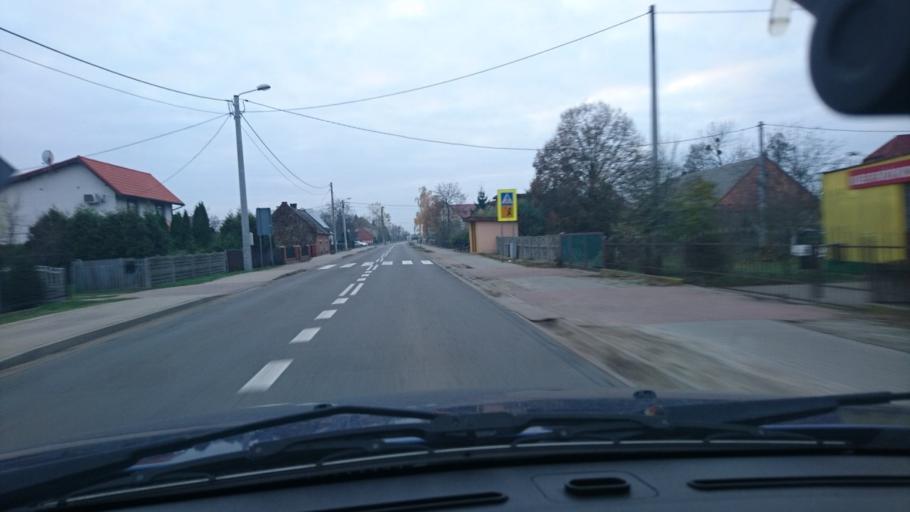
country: PL
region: Greater Poland Voivodeship
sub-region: Powiat ostrowski
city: Odolanow
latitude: 51.5421
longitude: 17.6535
